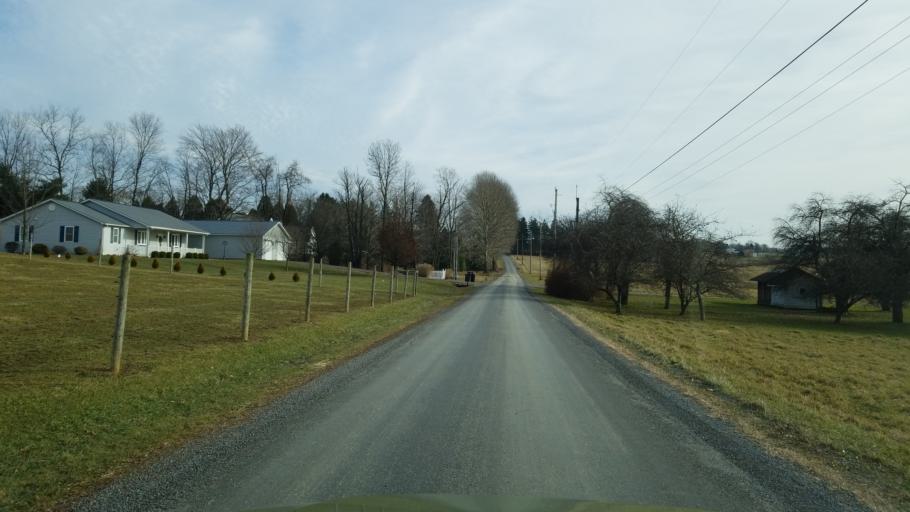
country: US
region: Pennsylvania
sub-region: Indiana County
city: Johnsonburg
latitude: 40.9395
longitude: -78.8794
